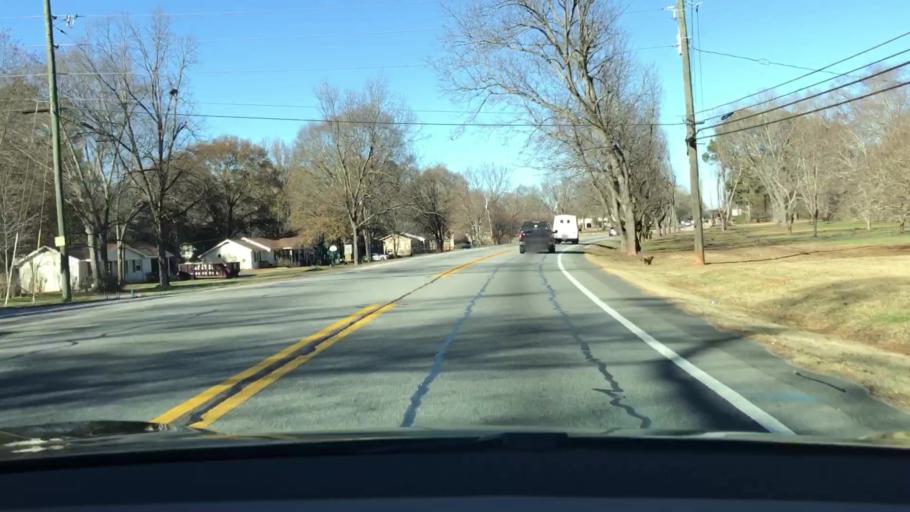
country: US
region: Georgia
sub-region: Walton County
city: Monroe
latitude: 33.8210
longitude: -83.7321
